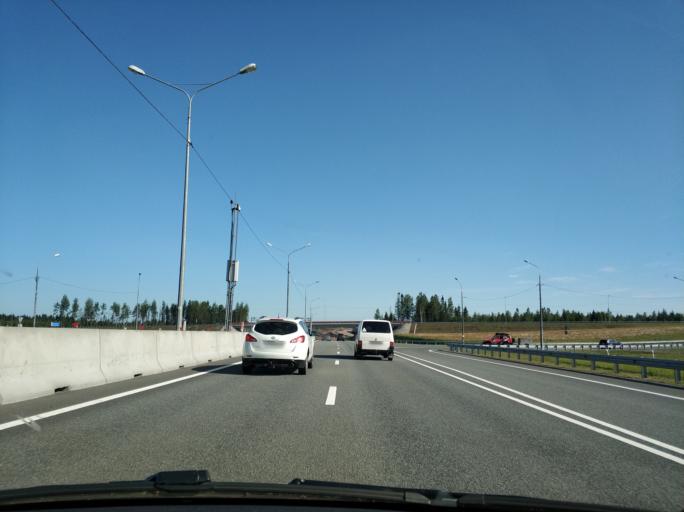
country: RU
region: Leningrad
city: Sosnovo
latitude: 60.5002
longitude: 30.1957
